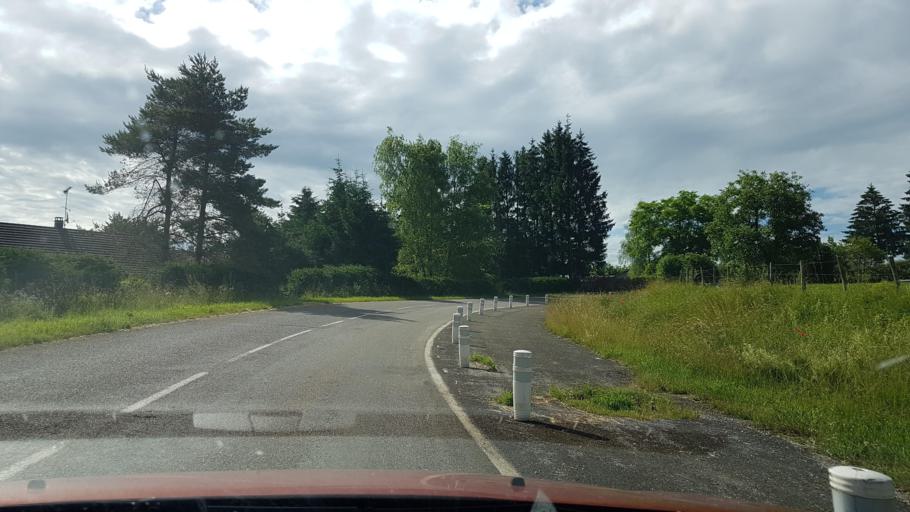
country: FR
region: Franche-Comte
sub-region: Departement du Jura
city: Clairvaux-les-Lacs
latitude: 46.5935
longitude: 5.7312
